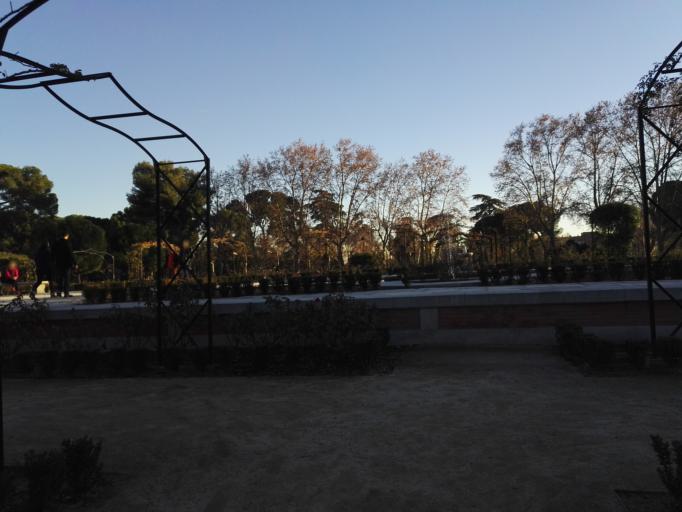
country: ES
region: Madrid
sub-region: Provincia de Madrid
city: Retiro
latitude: 40.4109
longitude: -3.6804
